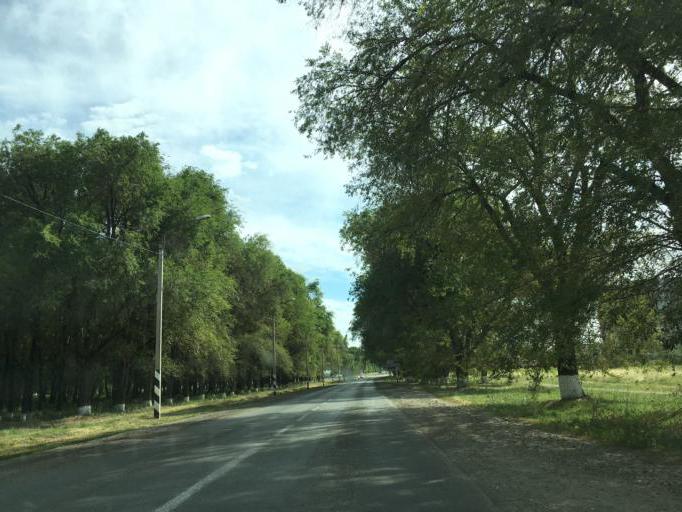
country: RU
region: Krasnodarskiy
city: Kushchevskaya
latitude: 46.5426
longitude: 39.6207
